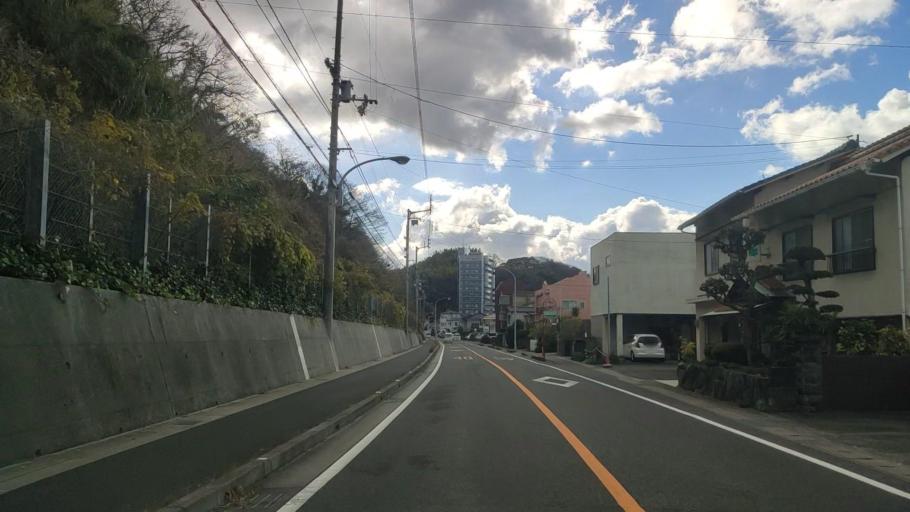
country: JP
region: Ehime
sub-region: Shikoku-chuo Shi
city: Matsuyama
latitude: 33.8727
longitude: 132.7094
